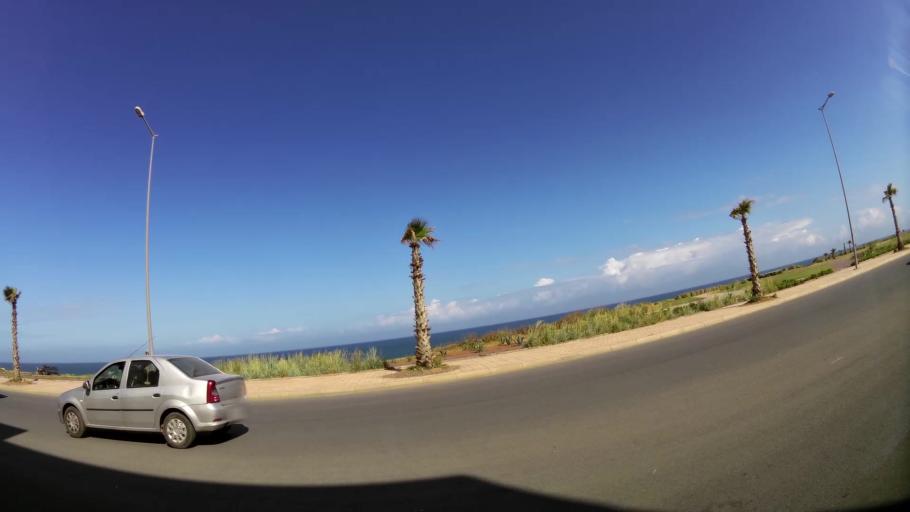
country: MA
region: Rabat-Sale-Zemmour-Zaer
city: Sale
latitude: 34.0660
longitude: -6.8072
